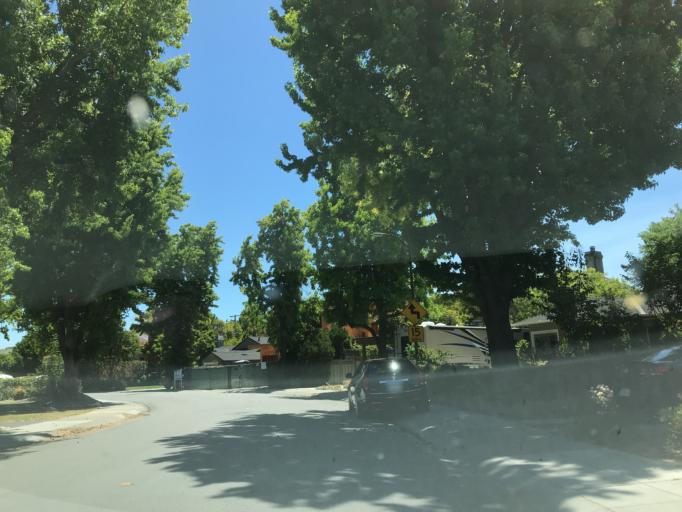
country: US
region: California
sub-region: Santa Clara County
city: Palo Alto
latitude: 37.4463
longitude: -122.1263
